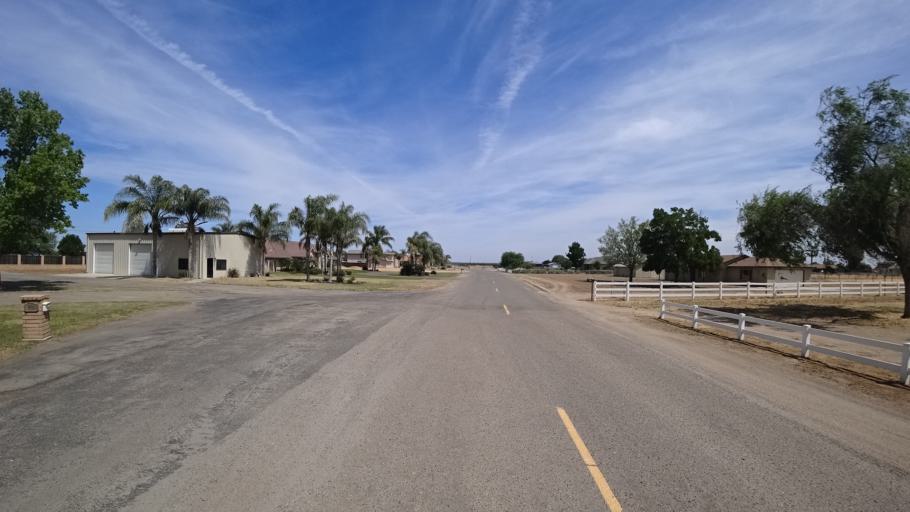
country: US
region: California
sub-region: Kings County
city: Home Garden
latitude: 36.3301
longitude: -119.5899
